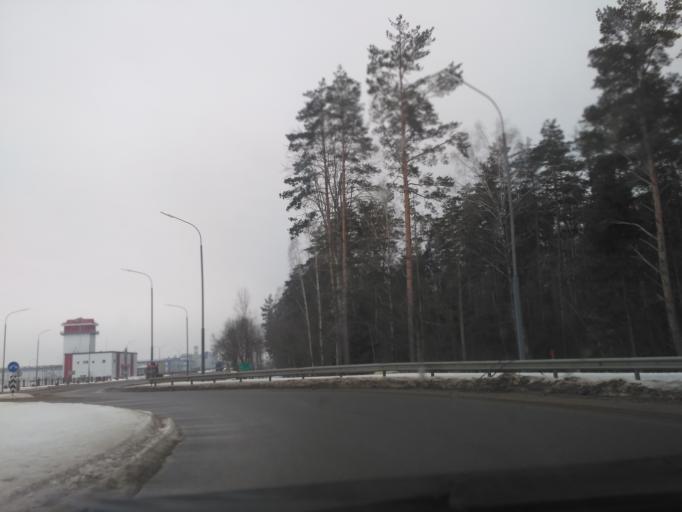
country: BY
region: Minsk
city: Horad Zhodzina
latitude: 54.1403
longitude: 28.3847
